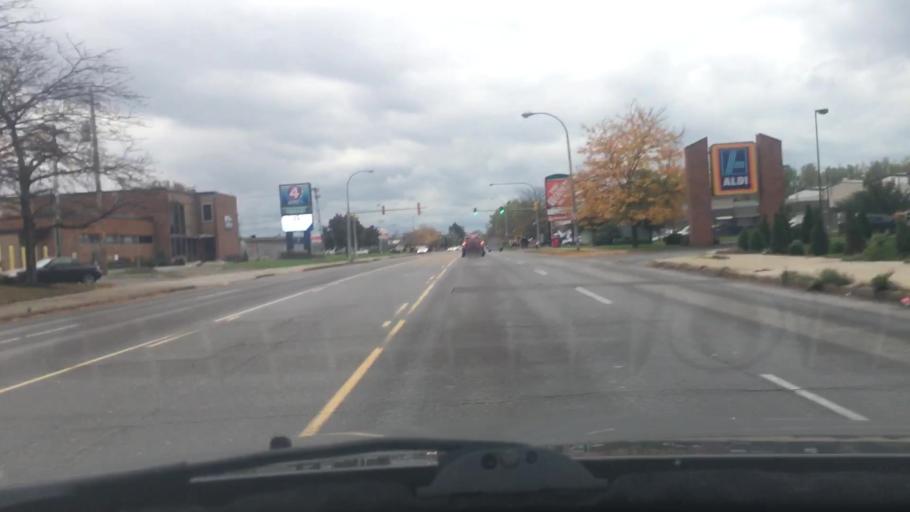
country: US
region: New York
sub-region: Erie County
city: Kenmore
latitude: 42.9545
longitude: -78.8783
